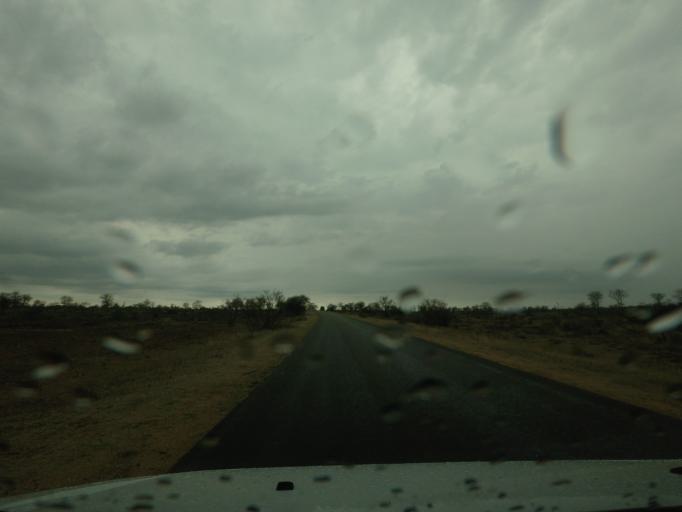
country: ZA
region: Limpopo
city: Thulamahashi
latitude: -24.4758
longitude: 31.3949
